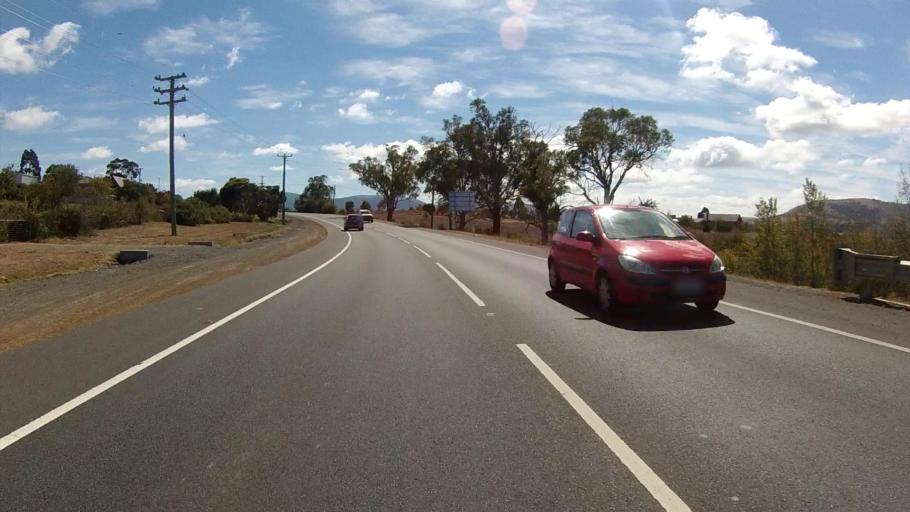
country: AU
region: Tasmania
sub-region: Brighton
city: Bridgewater
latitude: -42.7121
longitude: 147.2443
